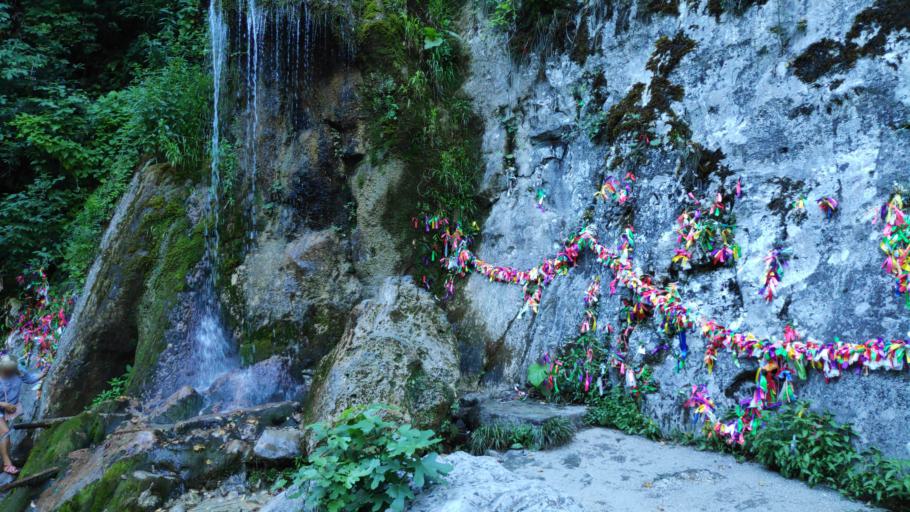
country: GE
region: Abkhazia
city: Gagra
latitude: 43.4336
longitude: 40.5297
